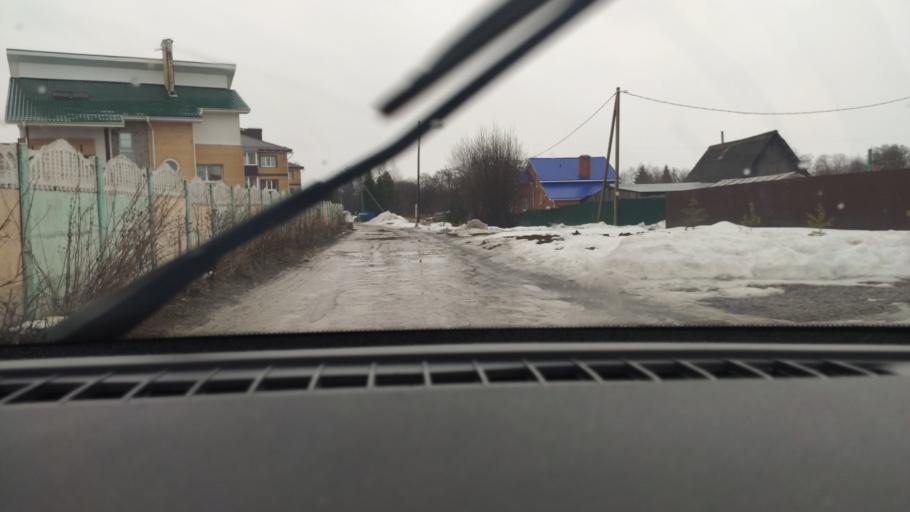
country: RU
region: Perm
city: Kultayevo
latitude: 57.8988
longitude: 55.9460
